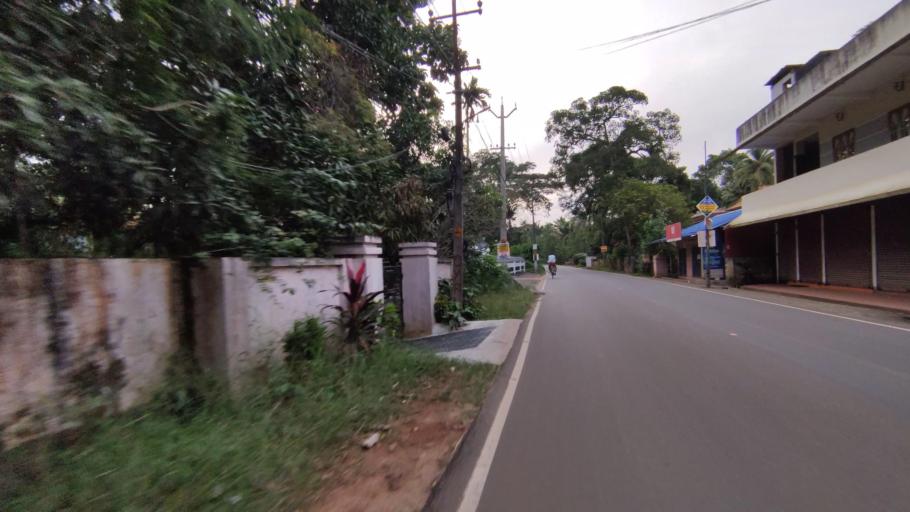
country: IN
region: Kerala
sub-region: Alappuzha
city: Shertallai
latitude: 9.6579
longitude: 76.3660
